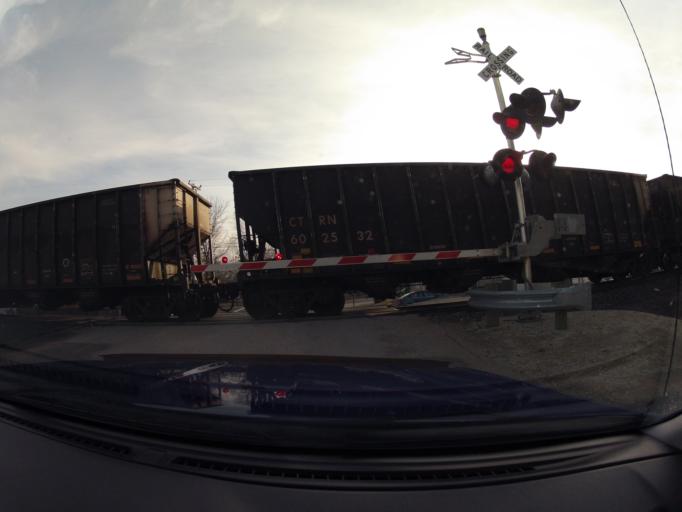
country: US
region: Kansas
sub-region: Pottawatomie County
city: Saint Marys
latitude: 39.1935
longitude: -96.0679
